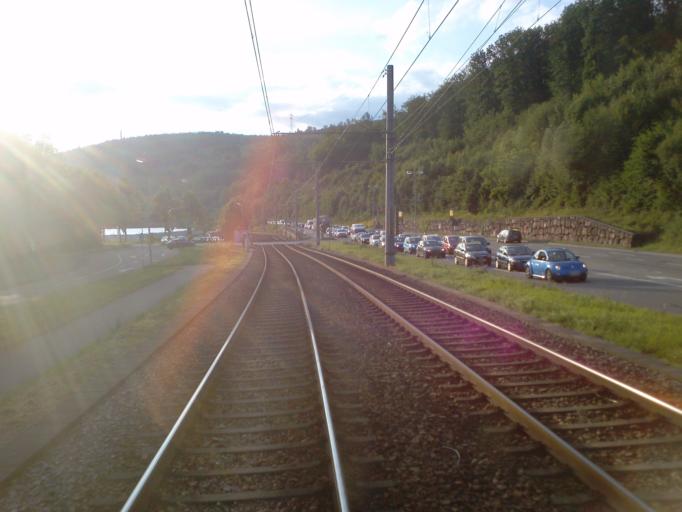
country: DE
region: Baden-Wuerttemberg
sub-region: Karlsruhe Region
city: Ettlingen
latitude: 48.9316
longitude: 8.4478
